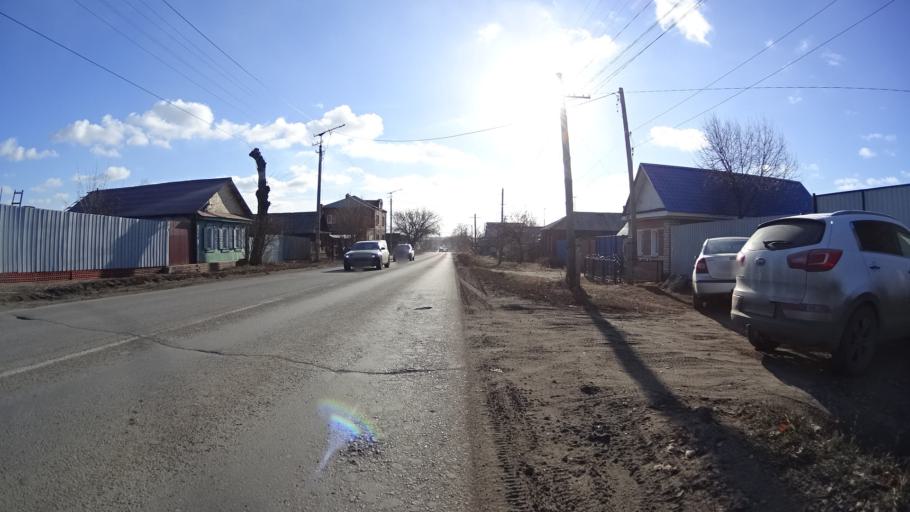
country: RU
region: Chelyabinsk
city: Troitsk
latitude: 54.0973
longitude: 61.5915
